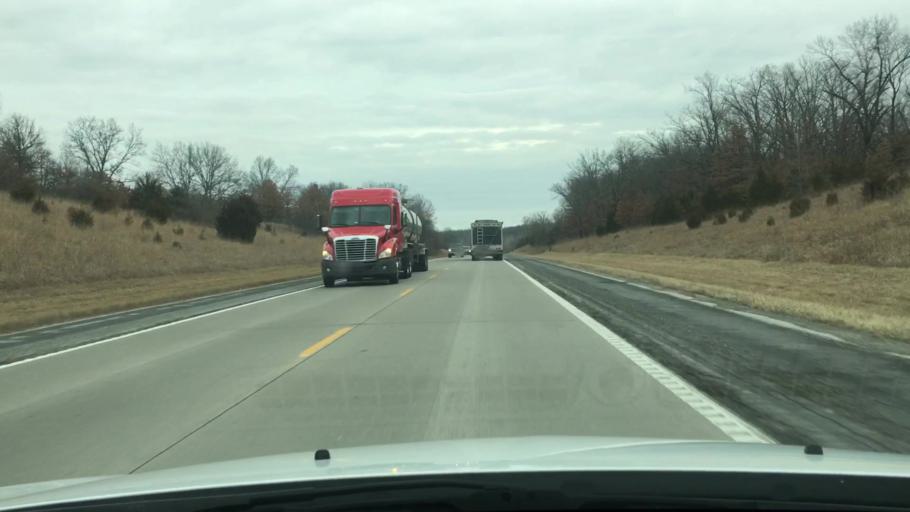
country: US
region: Missouri
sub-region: Audrain County
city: Mexico
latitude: 39.1392
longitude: -91.8503
